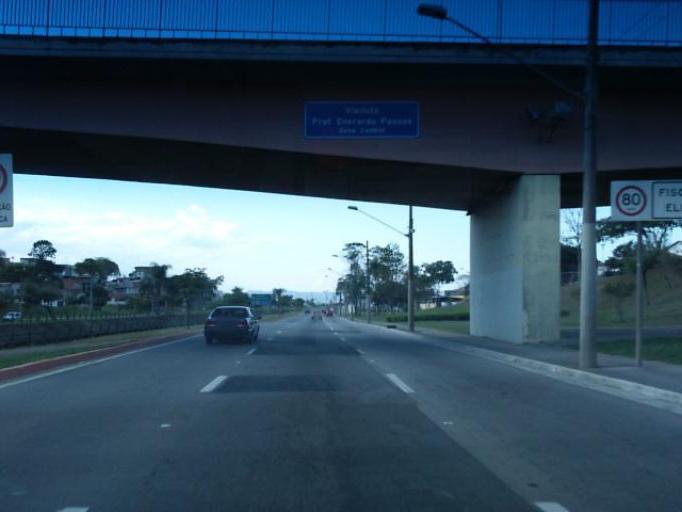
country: BR
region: Sao Paulo
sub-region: Sao Jose Dos Campos
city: Sao Jose dos Campos
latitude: -23.1807
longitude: -45.8767
